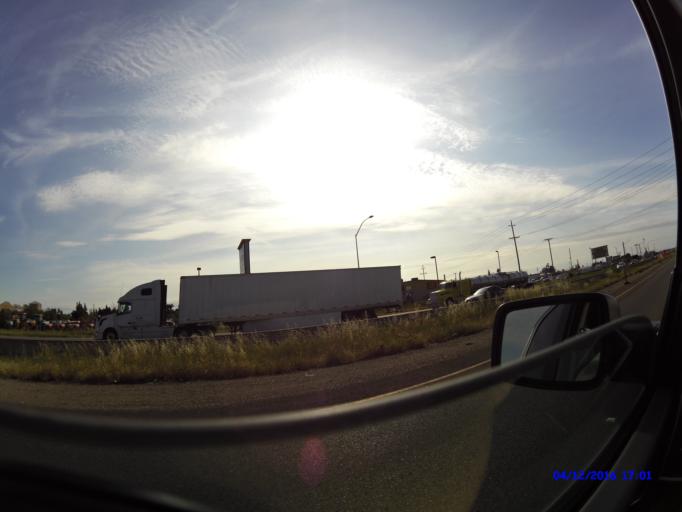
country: US
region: California
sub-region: Stanislaus County
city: Salida
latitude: 37.7031
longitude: -121.0742
